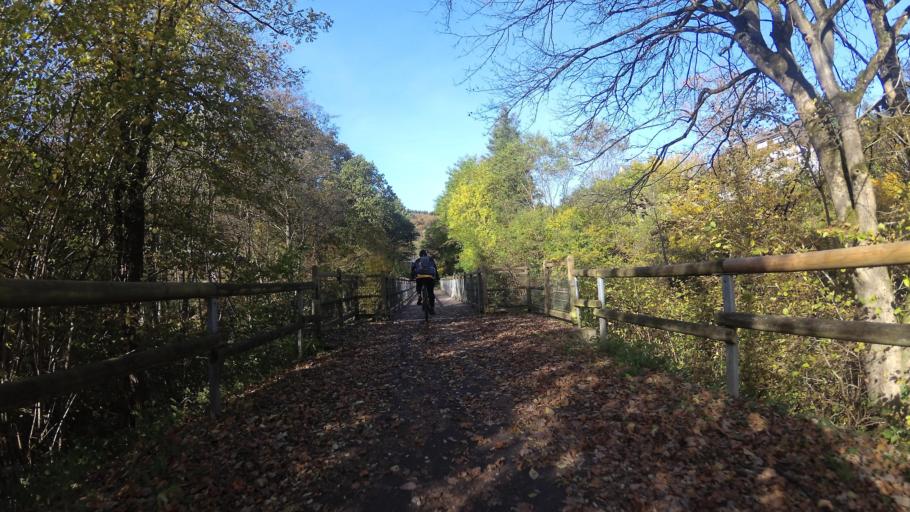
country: DE
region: Rheinland-Pfalz
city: Waldrach
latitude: 49.7407
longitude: 6.7431
